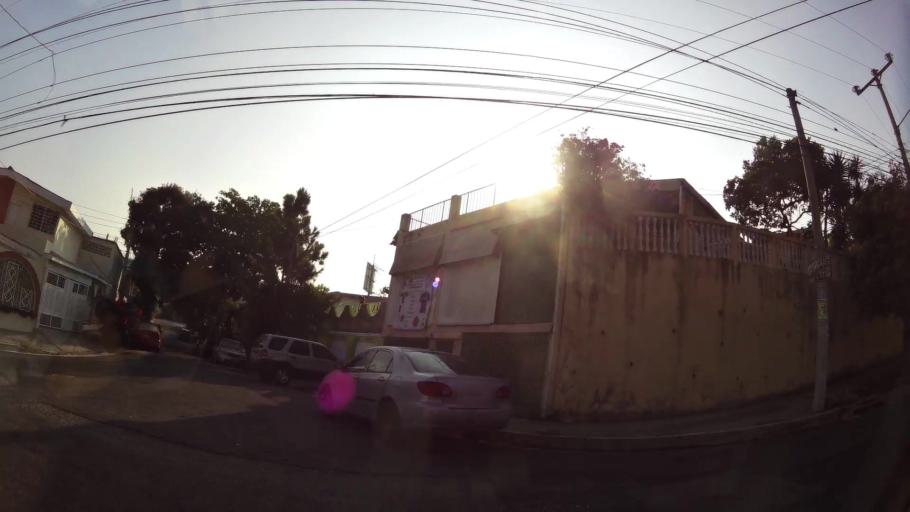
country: SV
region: La Libertad
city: Antiguo Cuscatlan
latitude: 13.6809
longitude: -89.2246
